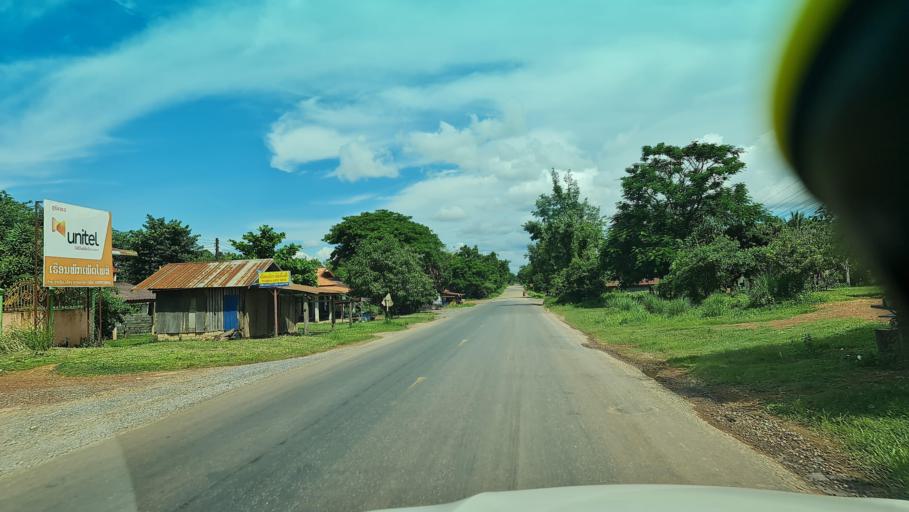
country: LA
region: Bolikhamxai
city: Ban Nahin
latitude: 18.2301
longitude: 104.1924
